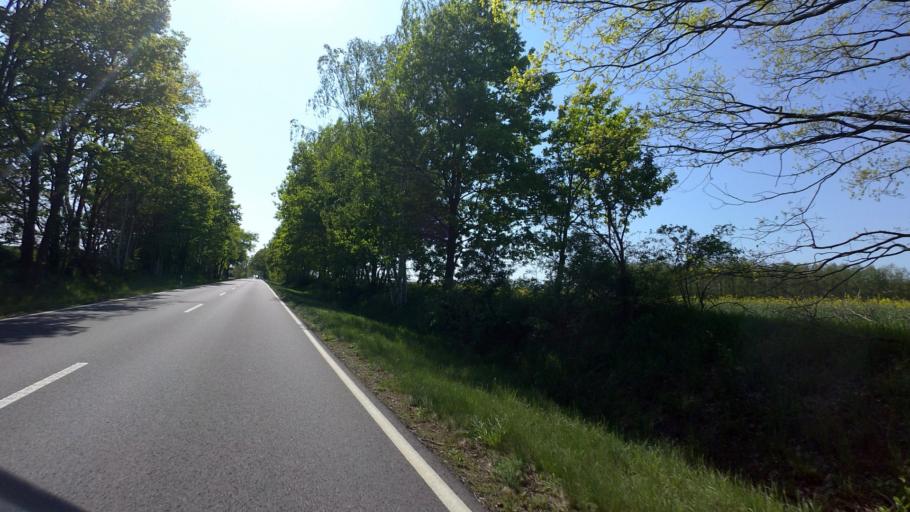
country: DE
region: Brandenburg
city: Neu Zauche
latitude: 52.0221
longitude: 14.0789
